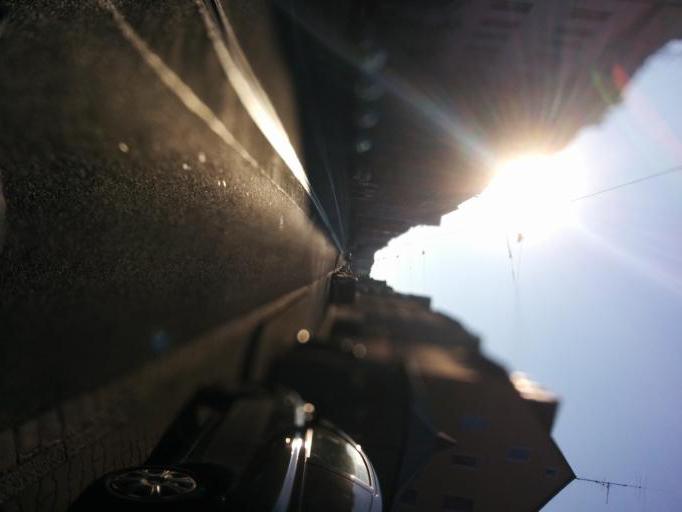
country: DE
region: Bavaria
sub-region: Regierungsbezirk Mittelfranken
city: Wetzendorf
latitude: 49.4611
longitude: 11.0527
